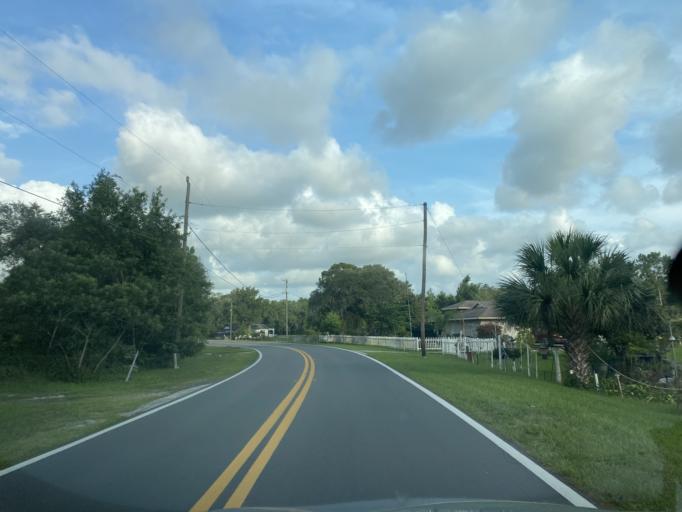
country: US
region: Florida
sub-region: Seminole County
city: Midway
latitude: 28.8464
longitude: -81.1734
